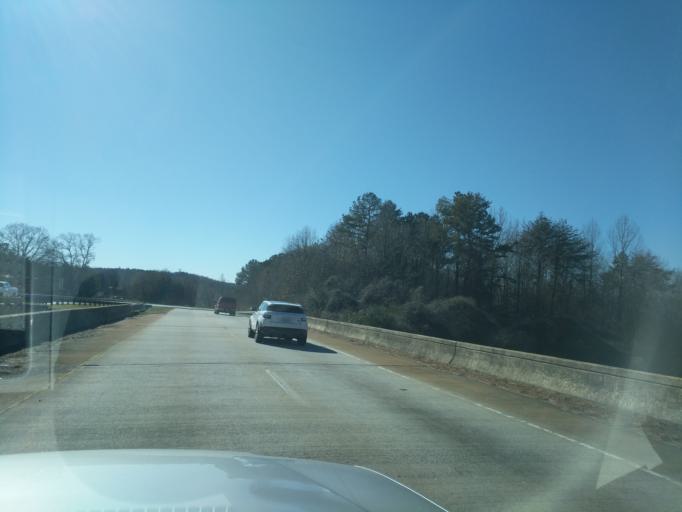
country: US
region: South Carolina
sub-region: Oconee County
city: Seneca
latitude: 34.6785
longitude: -83.0113
